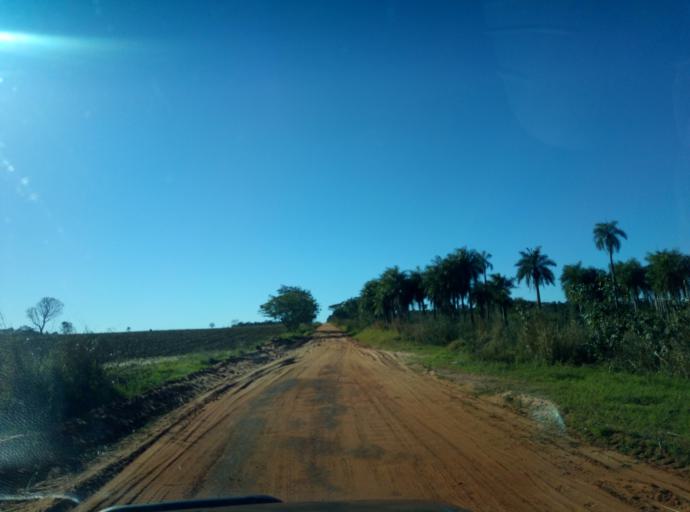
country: PY
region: Caaguazu
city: Doctor Cecilio Baez
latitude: -25.1608
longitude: -56.2782
